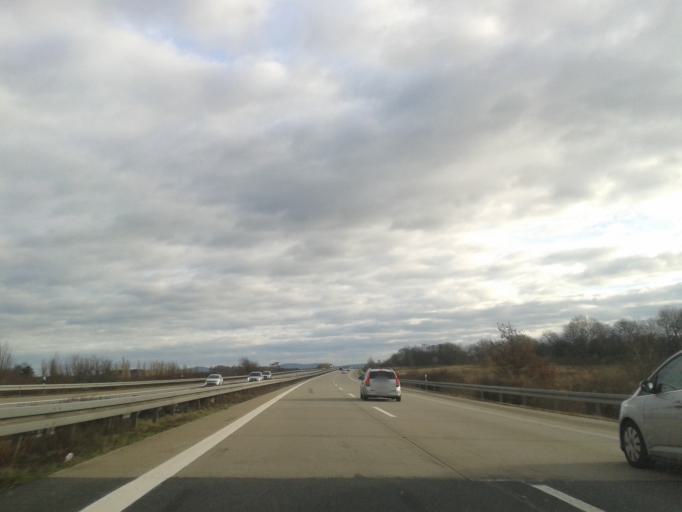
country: DE
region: Saxony
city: Weissenberg
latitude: 51.2106
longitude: 14.6300
